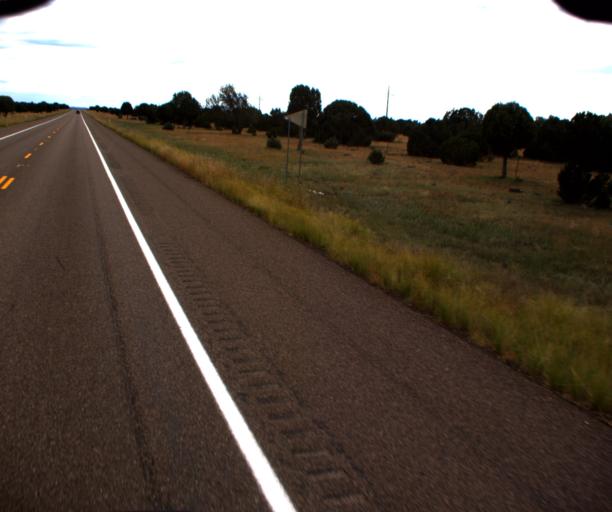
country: US
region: Arizona
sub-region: Navajo County
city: Show Low
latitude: 34.3041
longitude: -110.0365
